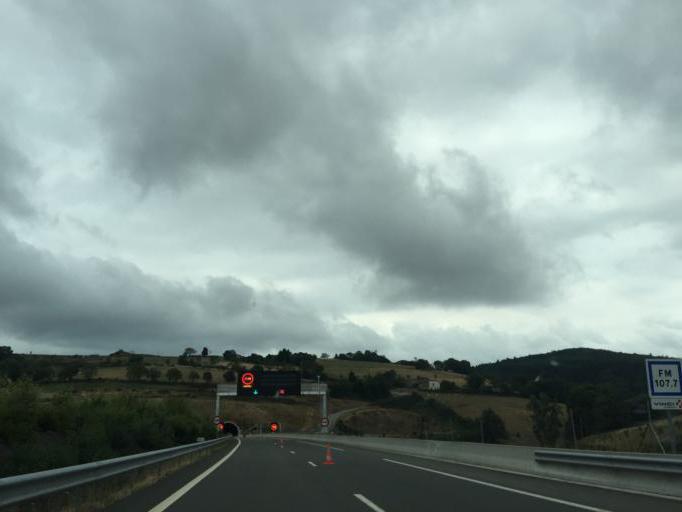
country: FR
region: Rhone-Alpes
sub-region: Departement de la Loire
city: Violay
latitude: 45.8604
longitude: 4.3228
